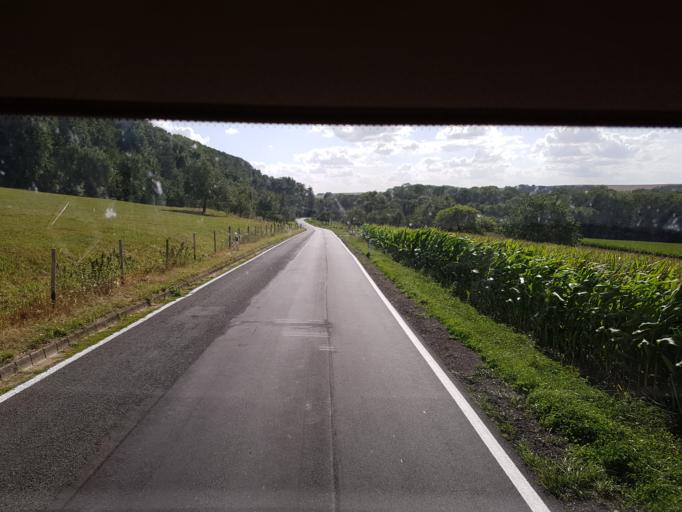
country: DE
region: Rheinland-Pfalz
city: Fisch
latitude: 49.6041
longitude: 6.5027
